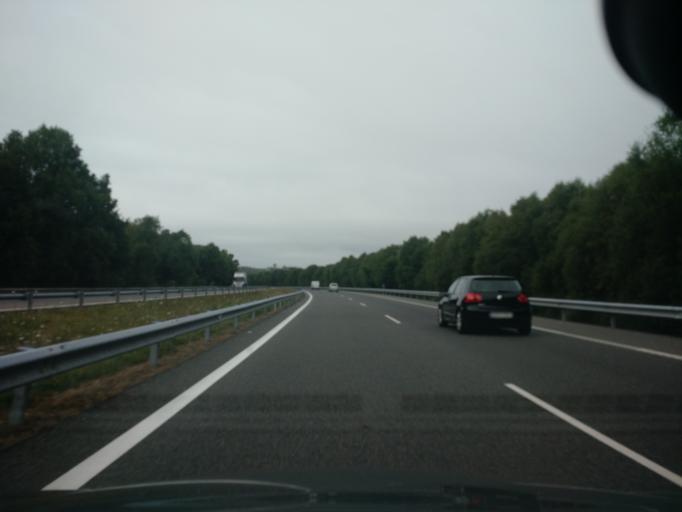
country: ES
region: Galicia
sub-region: Provincia da Coruna
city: Mesia
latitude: 43.1473
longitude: -8.3295
